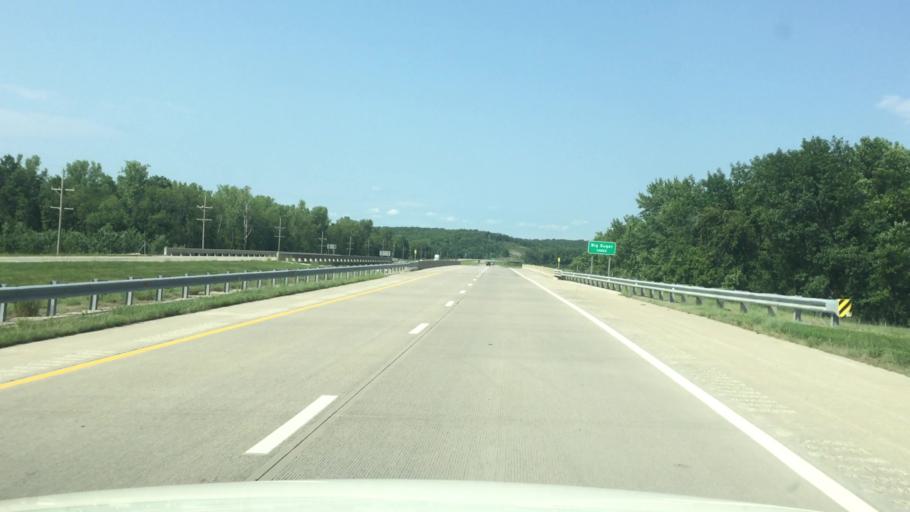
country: US
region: Kansas
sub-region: Linn County
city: Pleasanton
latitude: 38.2350
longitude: -94.6911
